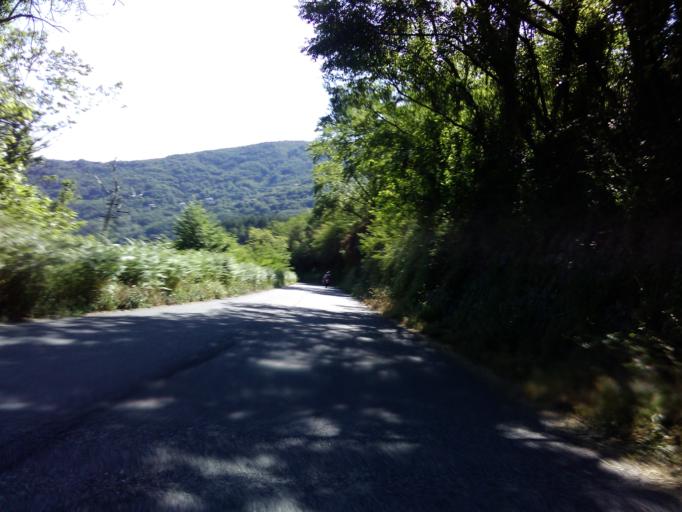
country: IT
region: Tuscany
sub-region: Provincia di Massa-Carrara
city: Comano
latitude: 44.3070
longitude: 10.0821
